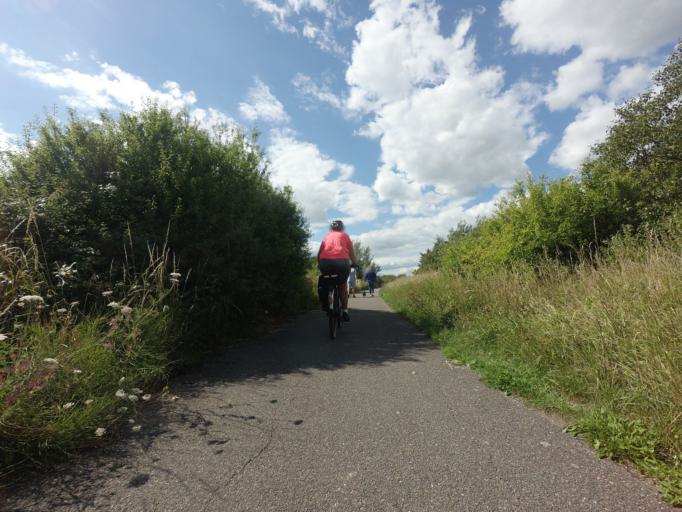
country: GB
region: England
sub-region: East Sussex
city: Eastbourne
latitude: 50.8078
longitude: 0.2806
